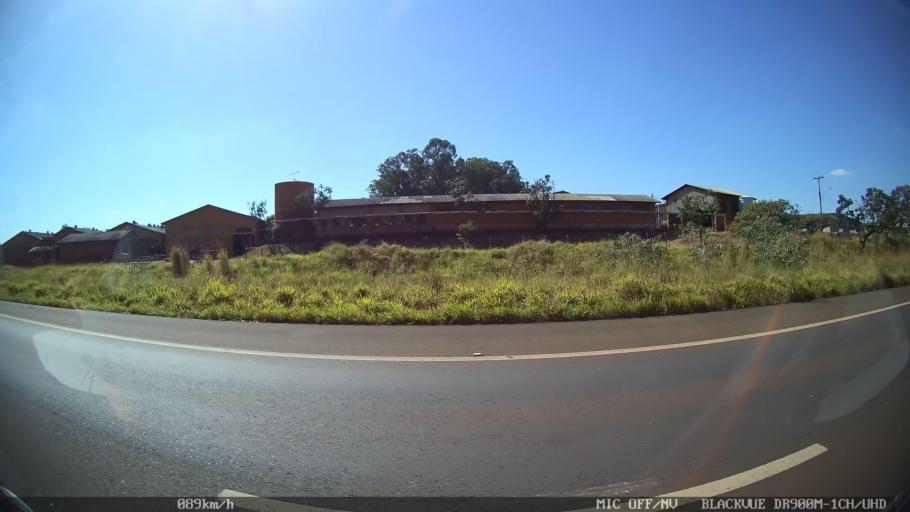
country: BR
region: Sao Paulo
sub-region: Franca
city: Franca
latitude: -20.5541
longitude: -47.4498
